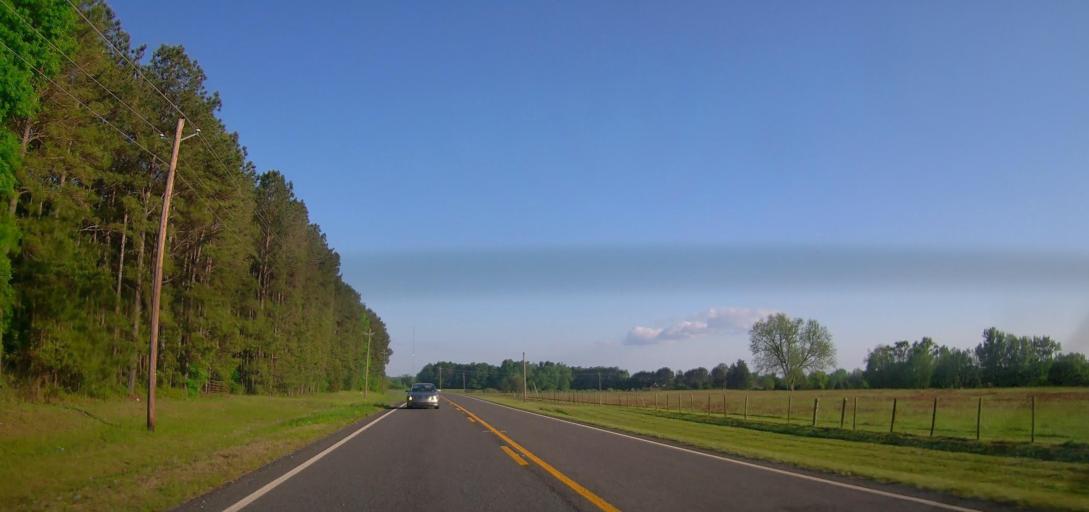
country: US
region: Georgia
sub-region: Jasper County
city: Monticello
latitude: 33.4522
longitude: -83.6297
